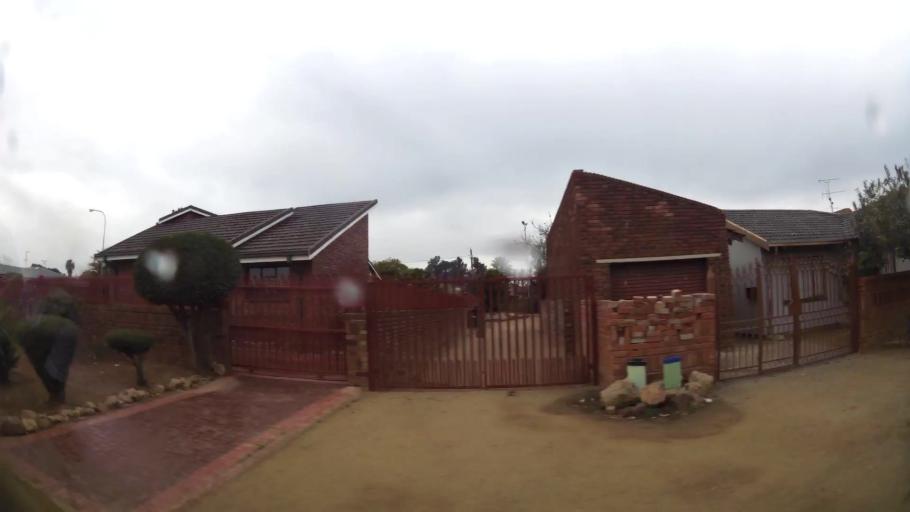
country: ZA
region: Gauteng
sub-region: City of Tshwane Metropolitan Municipality
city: Cullinan
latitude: -25.7194
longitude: 28.3618
